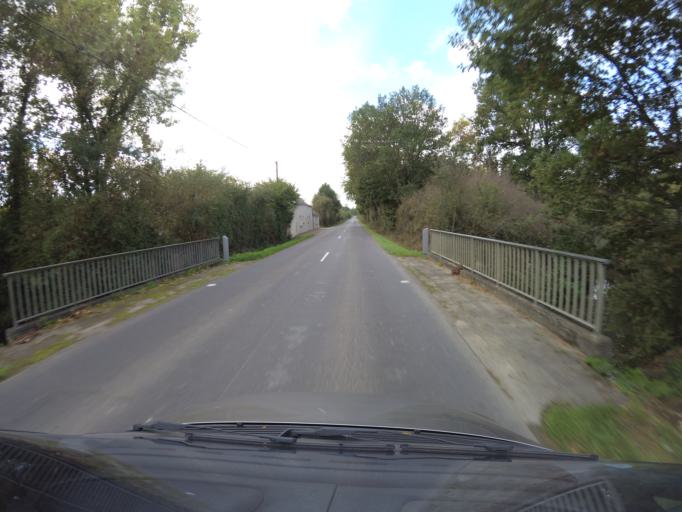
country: FR
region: Pays de la Loire
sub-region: Departement de la Loire-Atlantique
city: Heric
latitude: 47.4106
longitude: -1.6349
